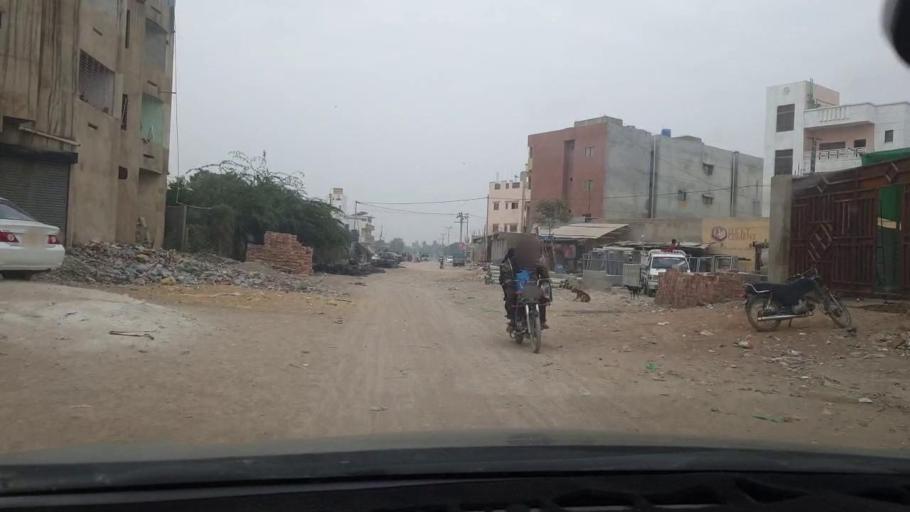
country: PK
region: Sindh
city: Malir Cantonment
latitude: 24.9216
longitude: 67.2601
